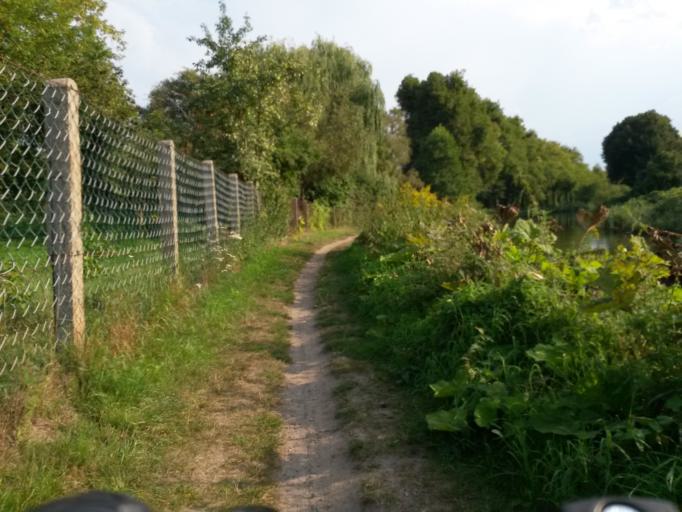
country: DE
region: Brandenburg
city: Templin
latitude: 53.1202
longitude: 13.4952
